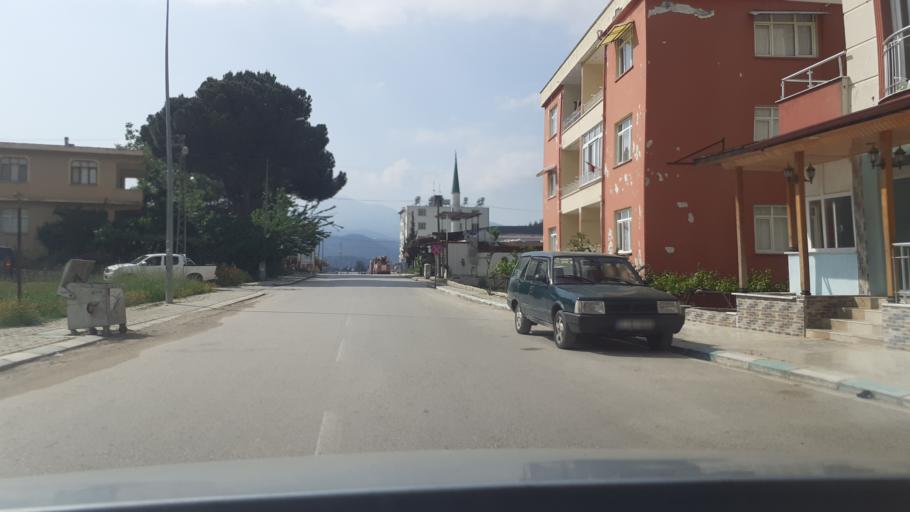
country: TR
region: Hatay
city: Yayladagi
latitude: 35.8995
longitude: 36.0720
